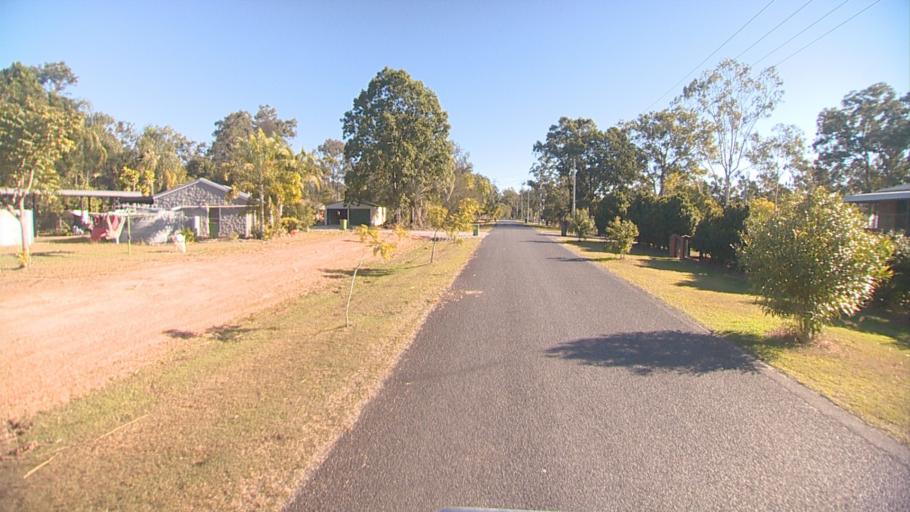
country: AU
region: Queensland
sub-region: Logan
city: Park Ridge South
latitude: -27.7314
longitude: 153.0253
